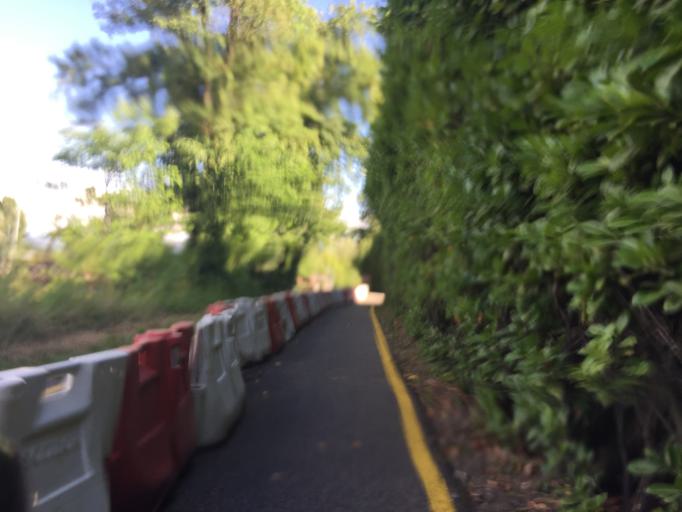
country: FR
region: Rhone-Alpes
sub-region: Departement de la Savoie
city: La Motte-Servolex
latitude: 45.5975
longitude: 5.8921
